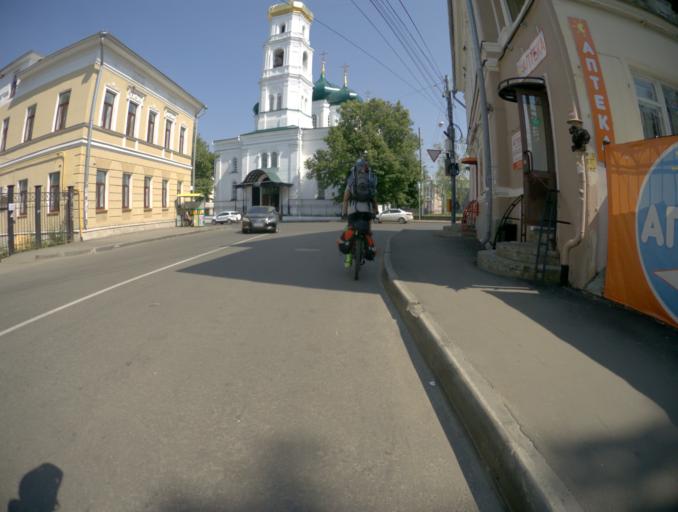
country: RU
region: Nizjnij Novgorod
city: Nizhniy Novgorod
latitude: 56.3216
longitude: 43.9897
